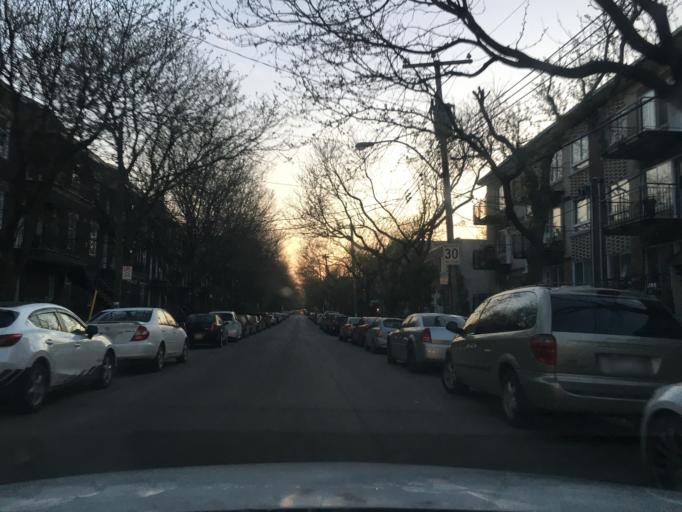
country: CA
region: Quebec
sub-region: Montreal
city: Montreal
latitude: 45.4786
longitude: -73.5534
